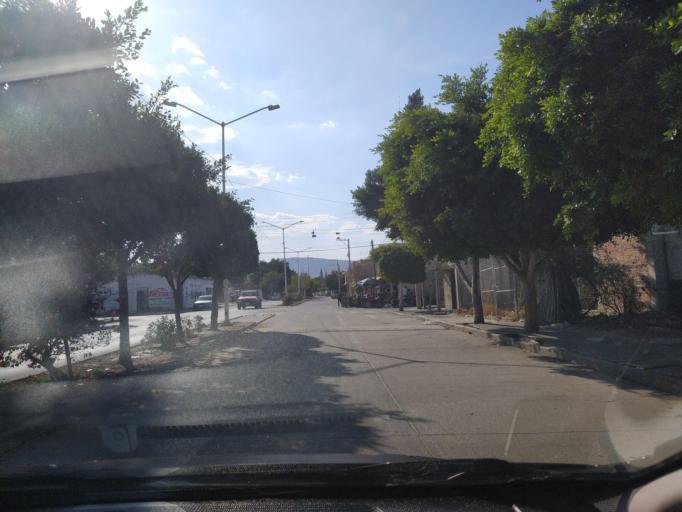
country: MX
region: Guanajuato
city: San Francisco del Rincon
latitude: 21.0174
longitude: -101.8450
